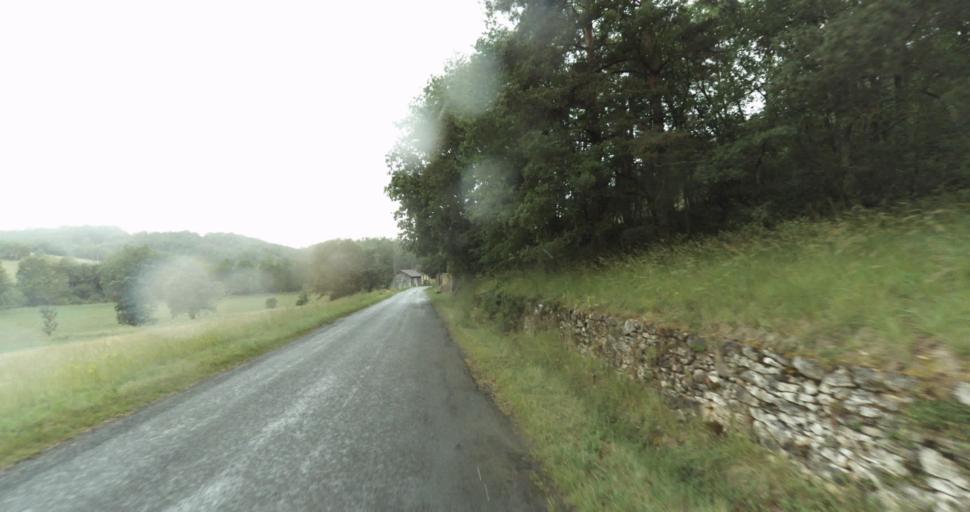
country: FR
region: Aquitaine
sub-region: Departement de la Dordogne
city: Beaumont-du-Perigord
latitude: 44.7673
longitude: 0.8029
